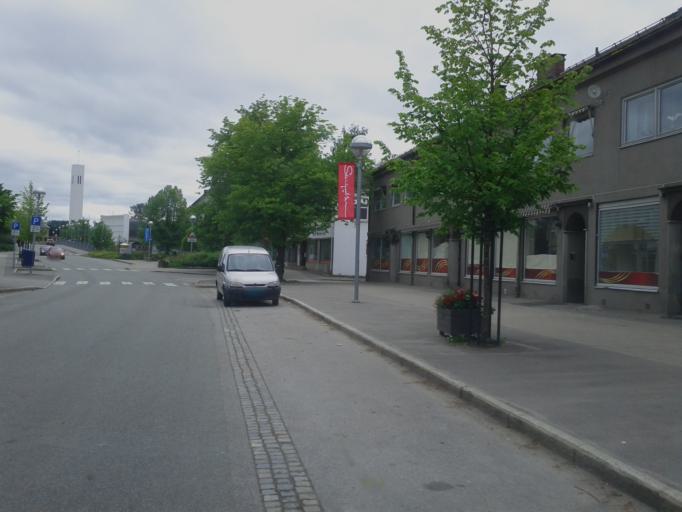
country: NO
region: Nord-Trondelag
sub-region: Steinkjer
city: Steinkjer
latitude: 64.0176
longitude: 11.4954
